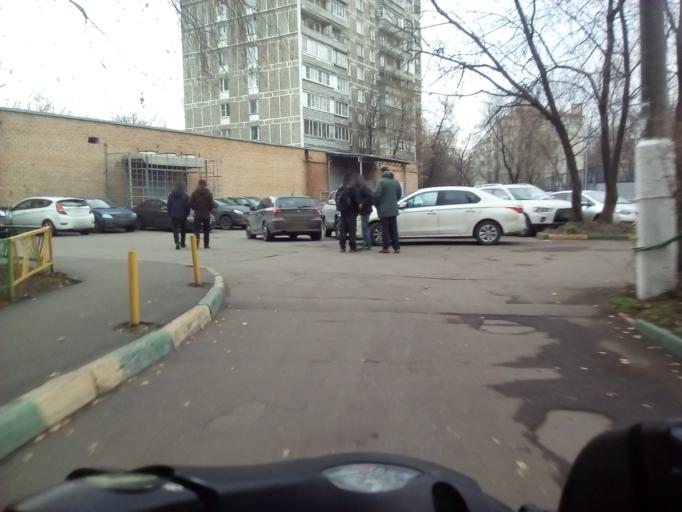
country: RU
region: Moscow
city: Lefortovo
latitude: 55.7719
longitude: 37.7130
